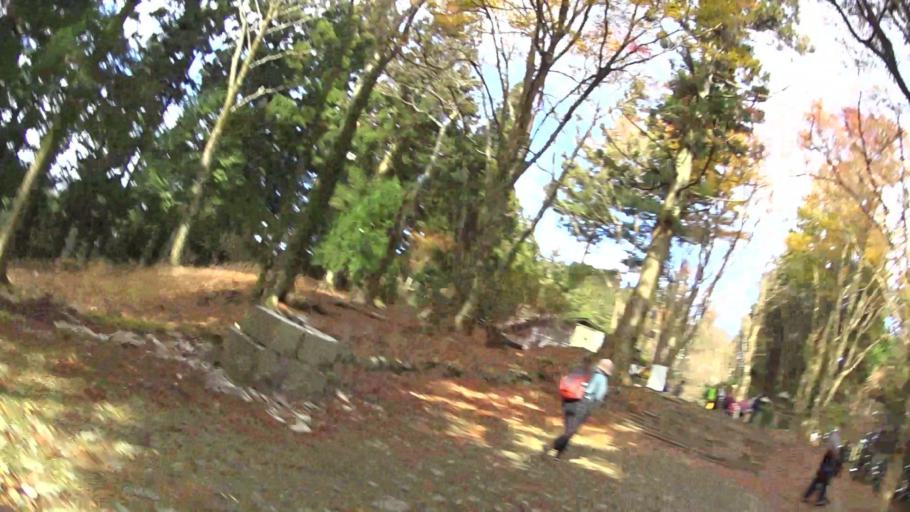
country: JP
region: Kyoto
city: Kameoka
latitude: 35.0577
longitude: 135.6343
